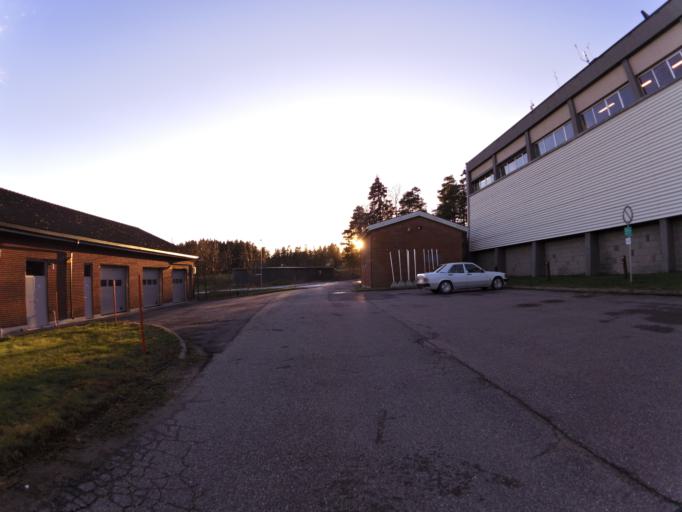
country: NO
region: Ostfold
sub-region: Fredrikstad
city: Fredrikstad
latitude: 59.2452
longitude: 10.9662
